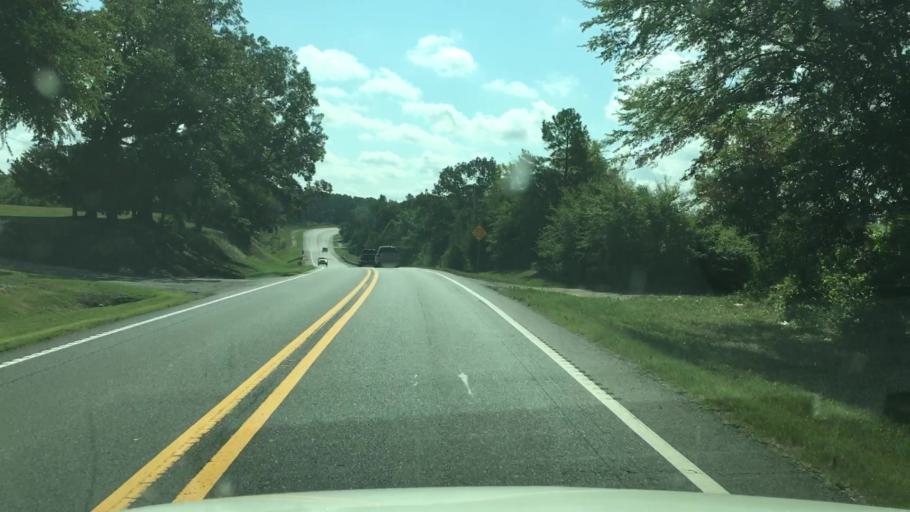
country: US
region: Arkansas
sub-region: Garland County
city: Piney
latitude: 34.5100
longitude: -93.2001
